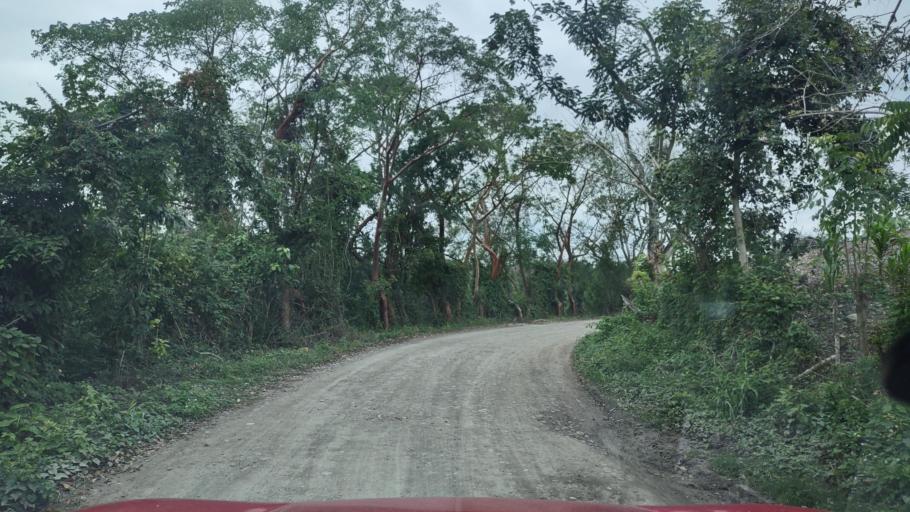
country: MX
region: Veracruz
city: Papantla de Olarte
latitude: 20.4211
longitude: -97.2724
